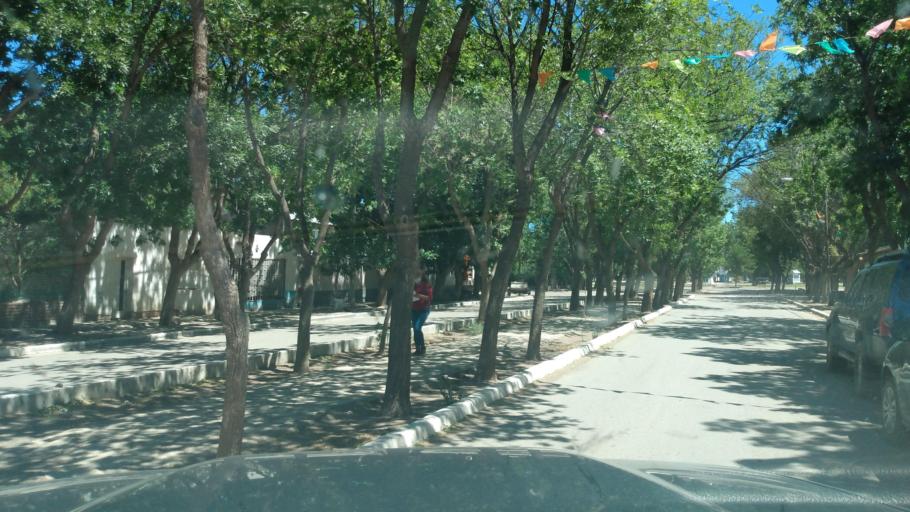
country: AR
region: Neuquen
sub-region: Departamento de Picun Leufu
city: Picun Leufu
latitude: -39.5195
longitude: -69.2898
